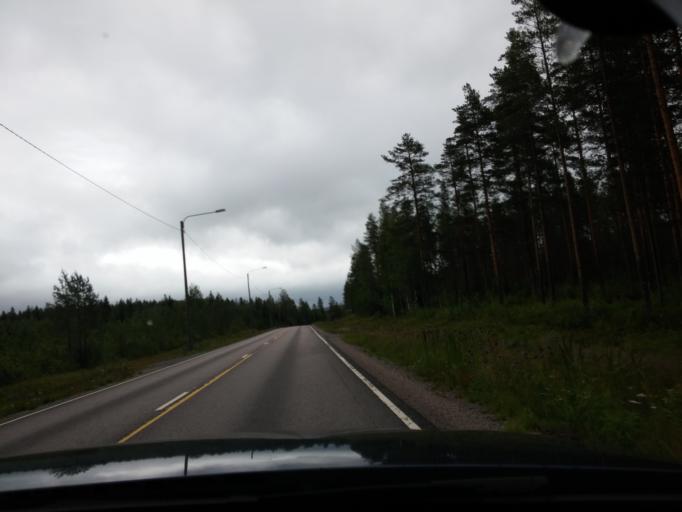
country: FI
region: Central Finland
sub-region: Saarijaervi-Viitasaari
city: Pylkoenmaeki
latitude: 62.6399
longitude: 24.8326
